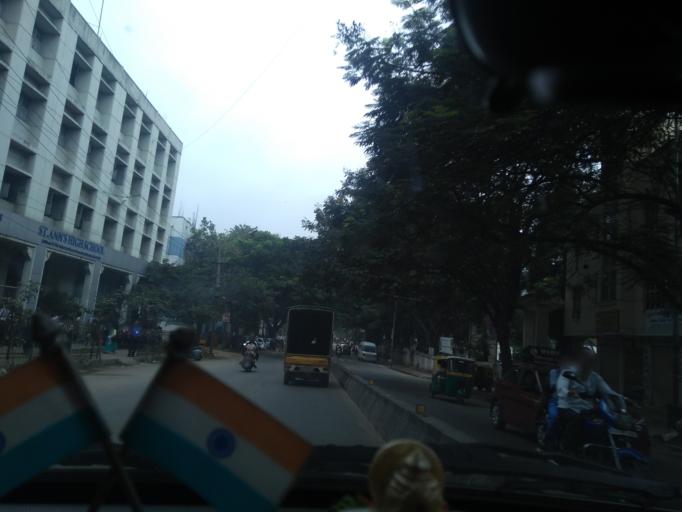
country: IN
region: Karnataka
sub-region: Bangalore Urban
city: Bangalore
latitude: 12.9804
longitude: 77.5568
